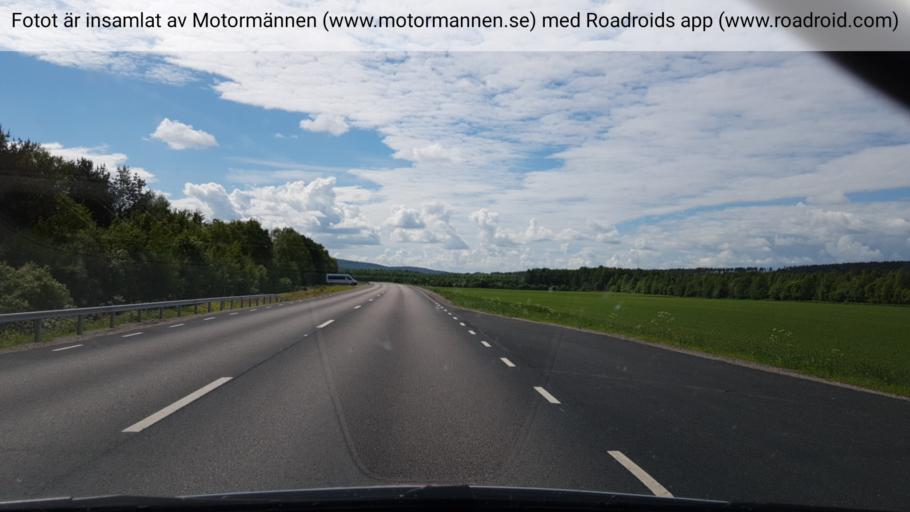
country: SE
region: Norrbotten
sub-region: Overtornea Kommun
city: OEvertornea
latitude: 66.4188
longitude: 23.6270
